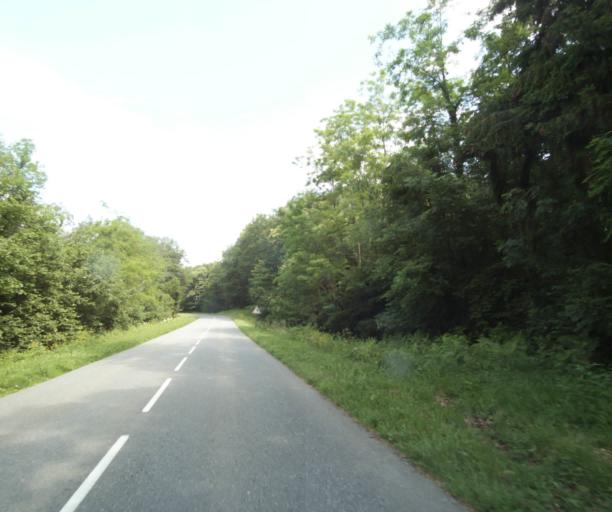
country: FR
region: Rhone-Alpes
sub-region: Departement de la Haute-Savoie
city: Armoy
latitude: 46.3615
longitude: 6.5081
